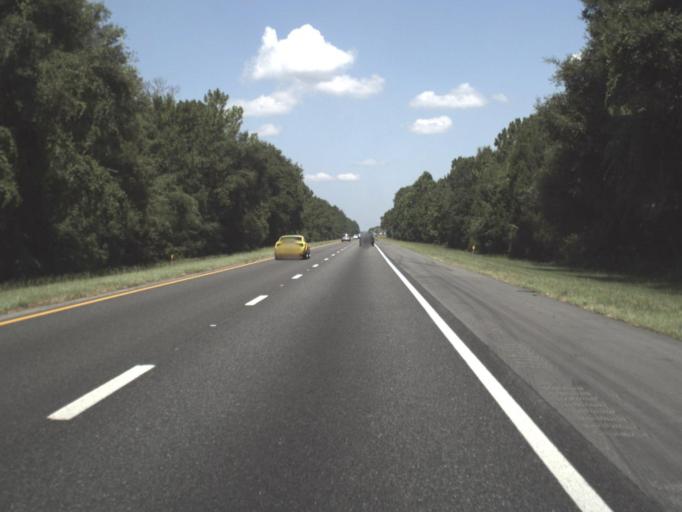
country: US
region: Florida
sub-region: Madison County
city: Madison
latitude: 30.3699
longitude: -83.2527
